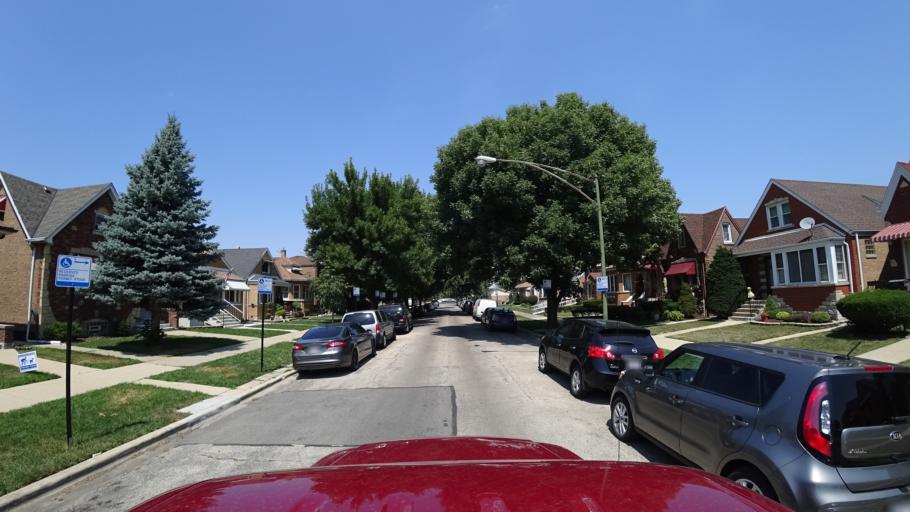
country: US
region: Illinois
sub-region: Cook County
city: Hometown
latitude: 41.7772
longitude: -87.7289
